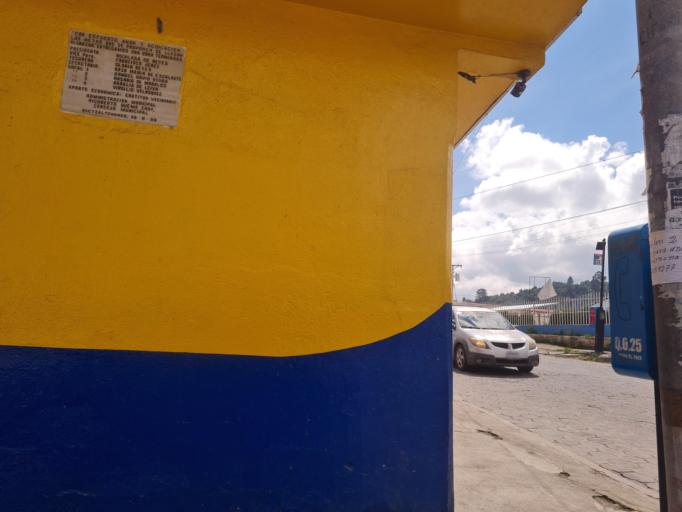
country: GT
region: Quetzaltenango
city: Quetzaltenango
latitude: 14.8329
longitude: -91.5301
